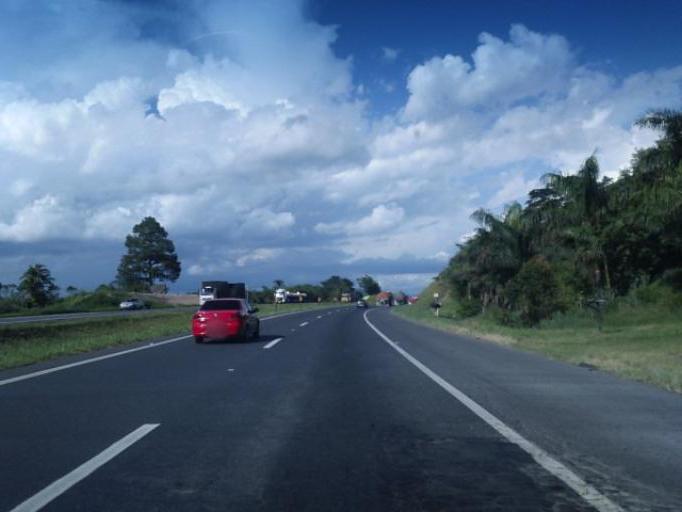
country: BR
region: Sao Paulo
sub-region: Juquia
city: Juquia
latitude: -24.3584
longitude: -47.6863
